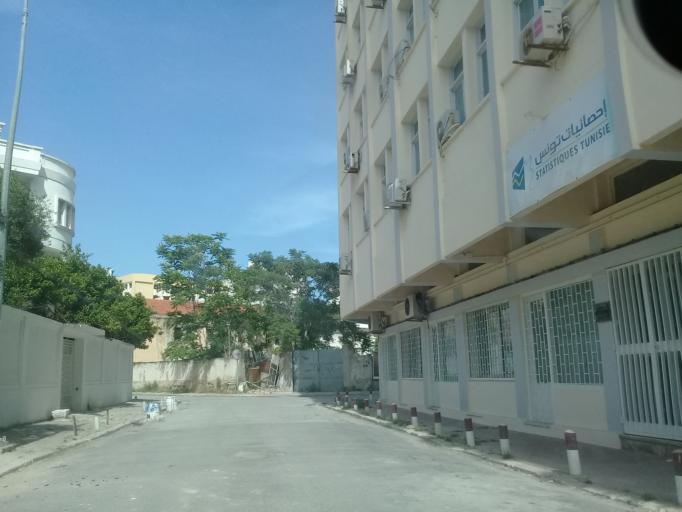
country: TN
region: Tunis
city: Tunis
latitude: 36.8165
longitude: 10.1809
